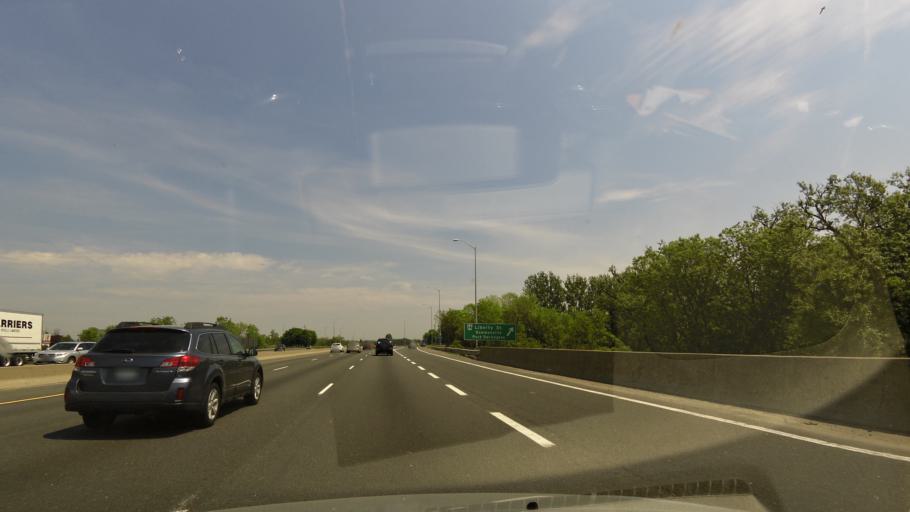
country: CA
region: Ontario
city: Oshawa
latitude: 43.8977
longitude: -78.6801
